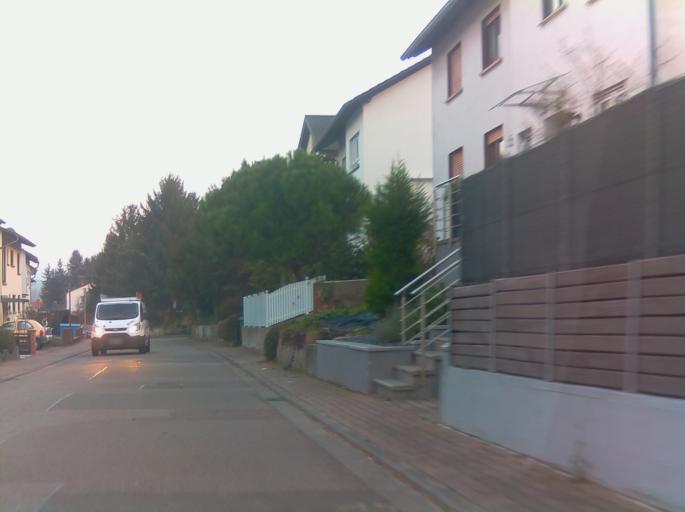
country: DE
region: Baden-Wuerttemberg
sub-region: Karlsruhe Region
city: Nussloch
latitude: 49.3229
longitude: 8.6903
